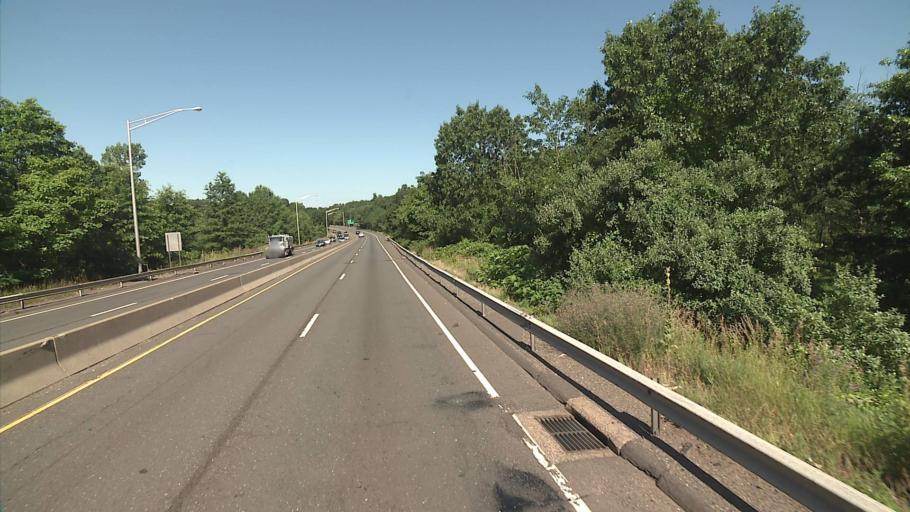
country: US
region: Connecticut
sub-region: Hartford County
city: Plainville
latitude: 41.6780
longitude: -72.8685
